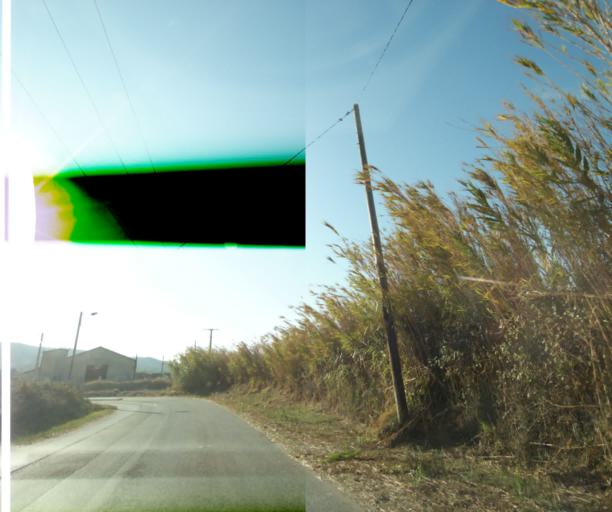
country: FR
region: Provence-Alpes-Cote d'Azur
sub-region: Departement des Bouches-du-Rhone
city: Chateauneuf-les-Martigues
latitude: 43.3989
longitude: 5.1335
